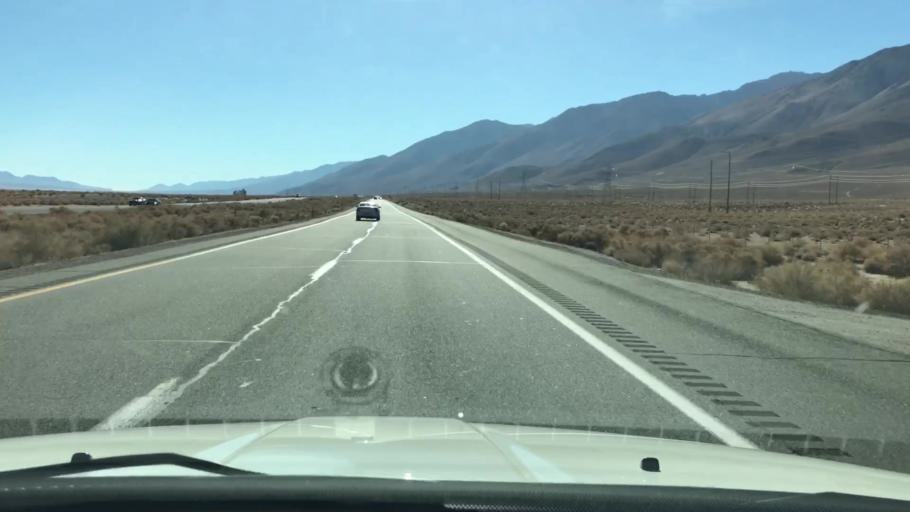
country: US
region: California
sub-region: Inyo County
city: Lone Pine
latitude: 36.4991
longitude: -118.0331
